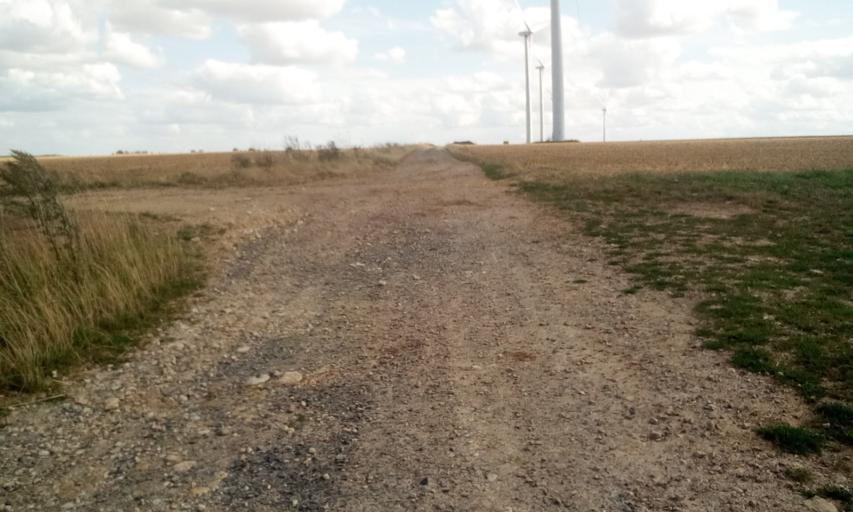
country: FR
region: Lower Normandy
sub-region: Departement du Calvados
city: Bellengreville
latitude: 49.1041
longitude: -0.2359
